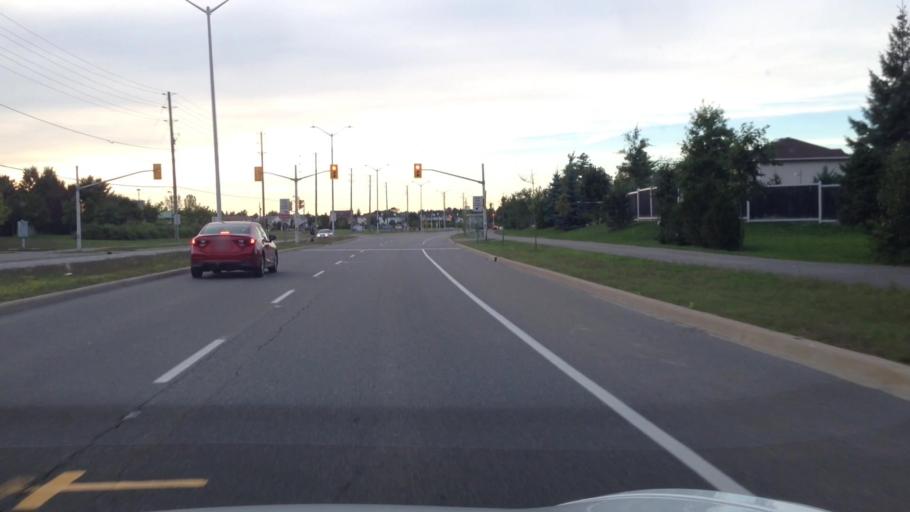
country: CA
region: Ontario
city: Clarence-Rockland
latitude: 45.4815
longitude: -75.4705
